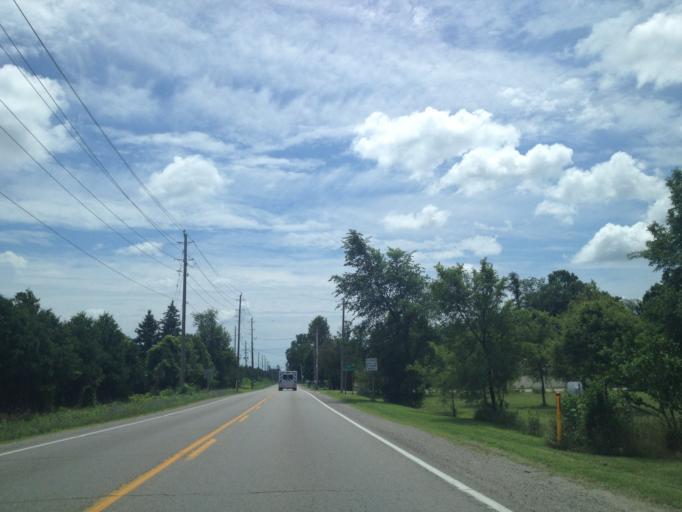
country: CA
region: Ontario
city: Norfolk County
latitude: 42.8379
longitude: -80.3424
